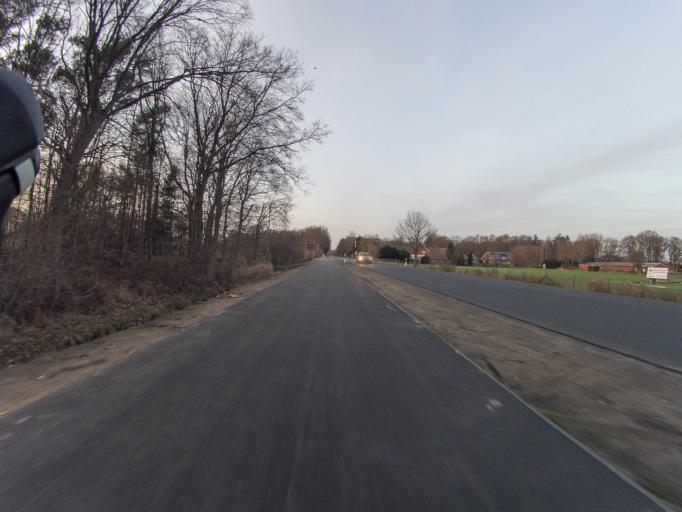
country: DE
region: North Rhine-Westphalia
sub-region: Regierungsbezirk Munster
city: Wettringen
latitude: 52.1994
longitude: 7.3236
